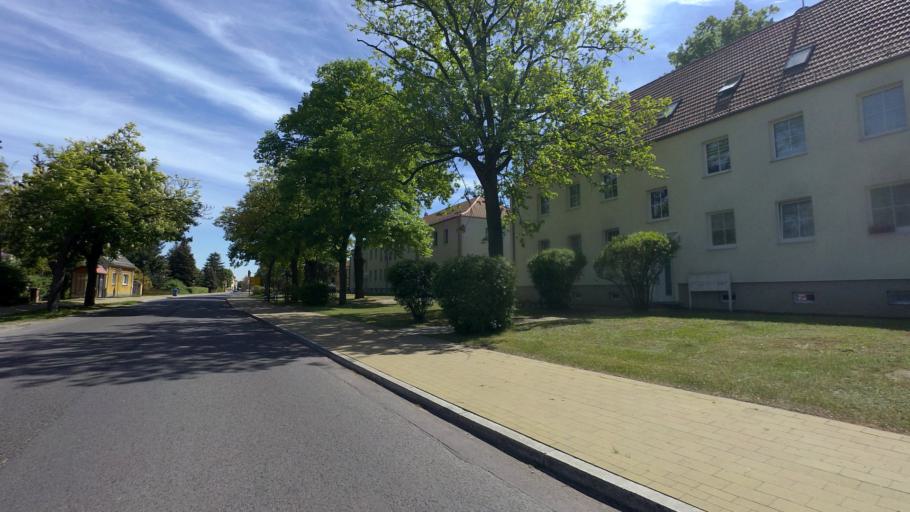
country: DE
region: Brandenburg
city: Baruth
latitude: 52.0464
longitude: 13.4971
